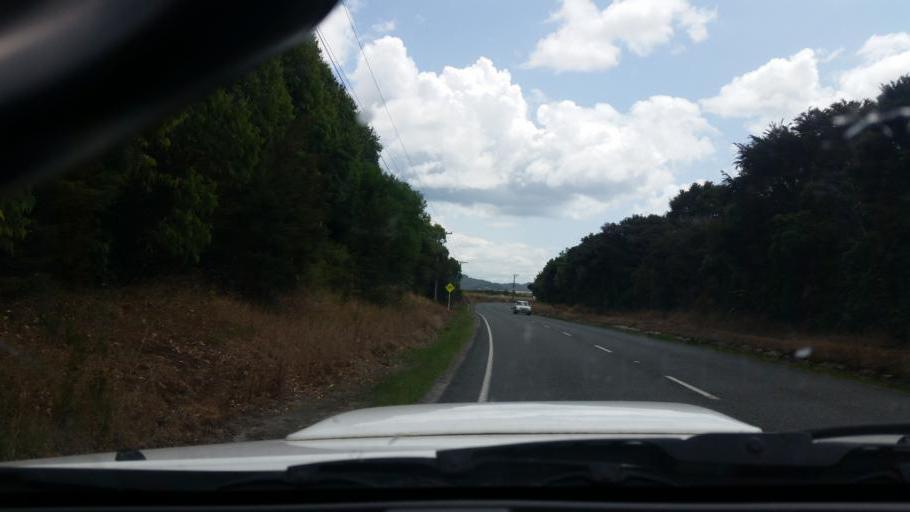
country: NZ
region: Auckland
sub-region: Auckland
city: Wellsford
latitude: -36.1149
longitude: 174.5750
